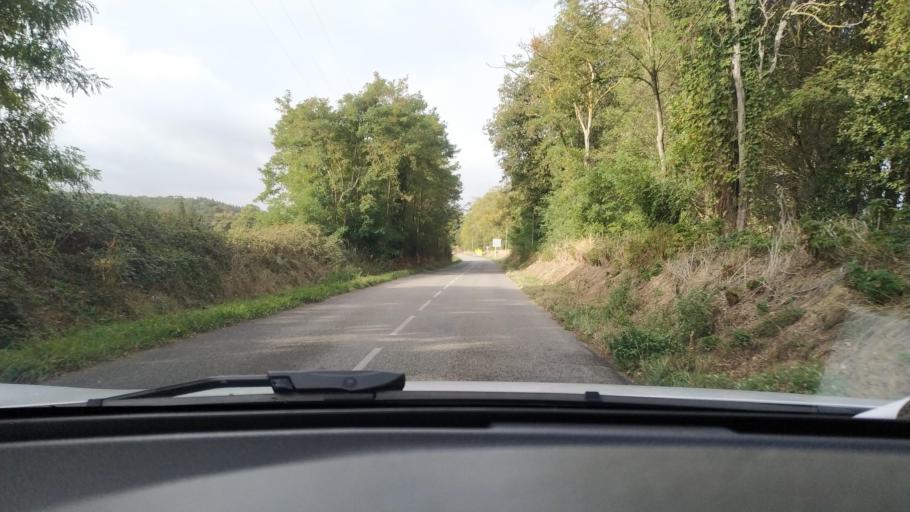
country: FR
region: Midi-Pyrenees
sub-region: Departement de la Haute-Garonne
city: Auterive
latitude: 43.3282
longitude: 1.4442
